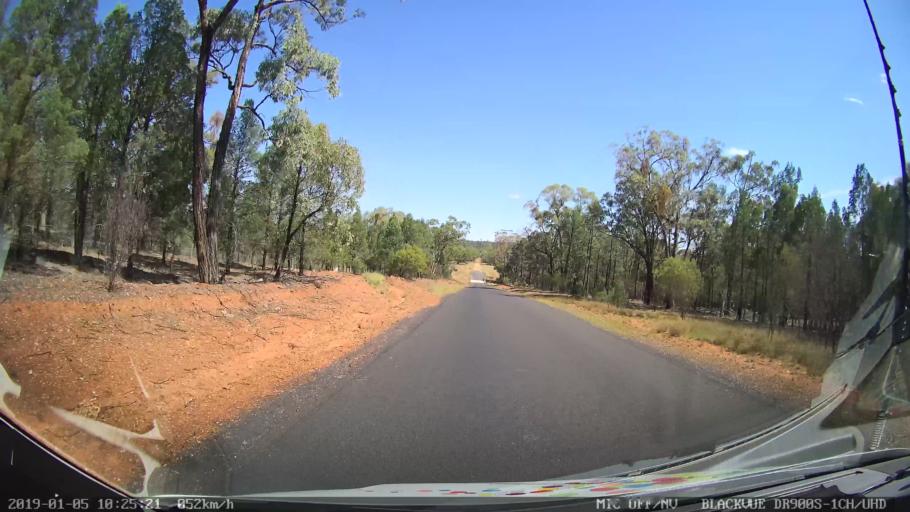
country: AU
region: New South Wales
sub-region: Gilgandra
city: Gilgandra
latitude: -31.5620
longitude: 148.9598
